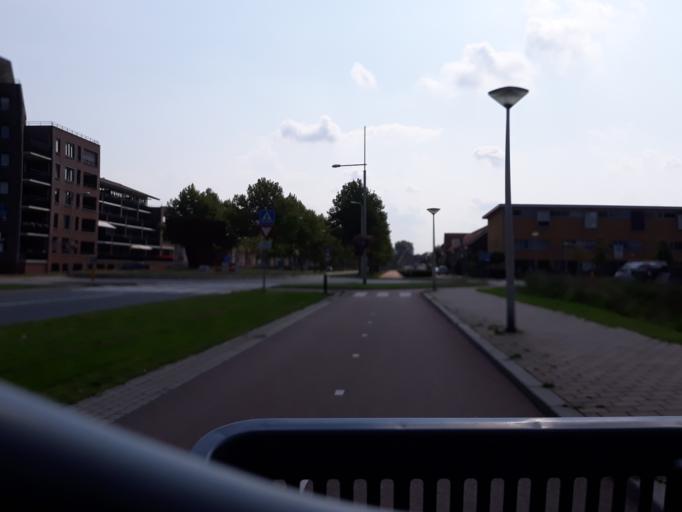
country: NL
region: South Holland
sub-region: Gemeente Hendrik-Ido-Ambacht
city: Hendrik-Ido-Ambacht
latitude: 51.8338
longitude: 4.6490
